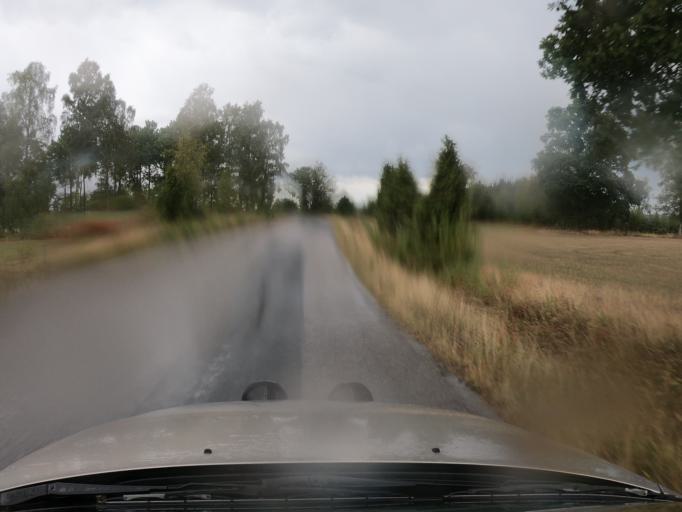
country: SE
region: Joenkoeping
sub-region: Vetlanda Kommun
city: Landsbro
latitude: 57.2548
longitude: 14.8316
